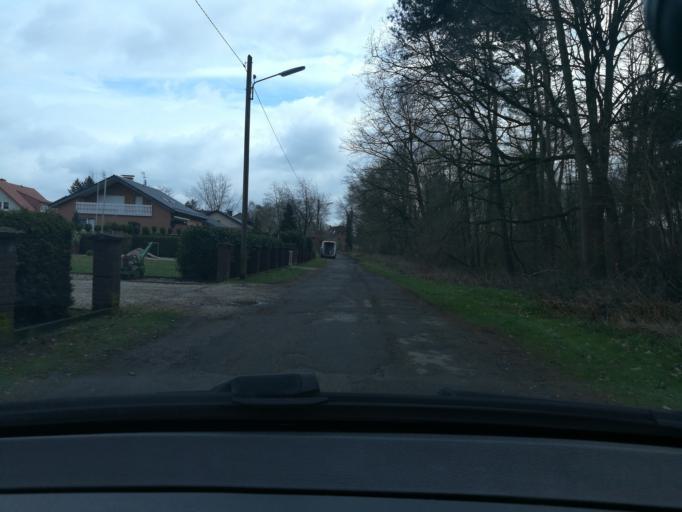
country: DE
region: North Rhine-Westphalia
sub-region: Regierungsbezirk Detmold
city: Verl
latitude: 51.9212
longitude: 8.5792
